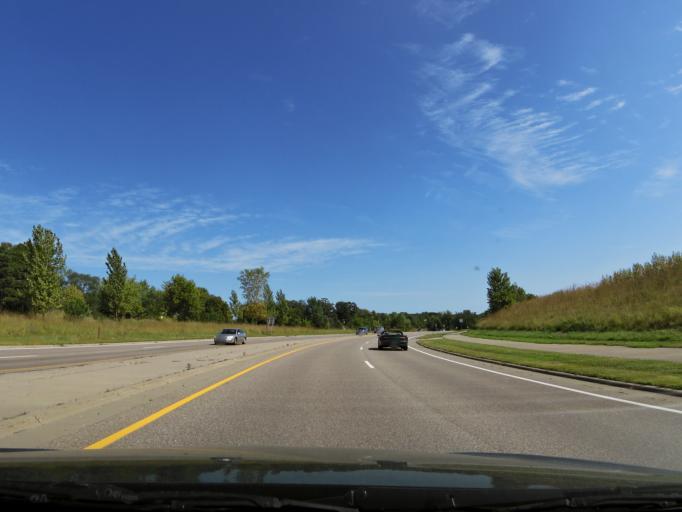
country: US
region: Minnesota
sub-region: Carver County
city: Chanhassen
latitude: 44.8474
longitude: -93.5386
